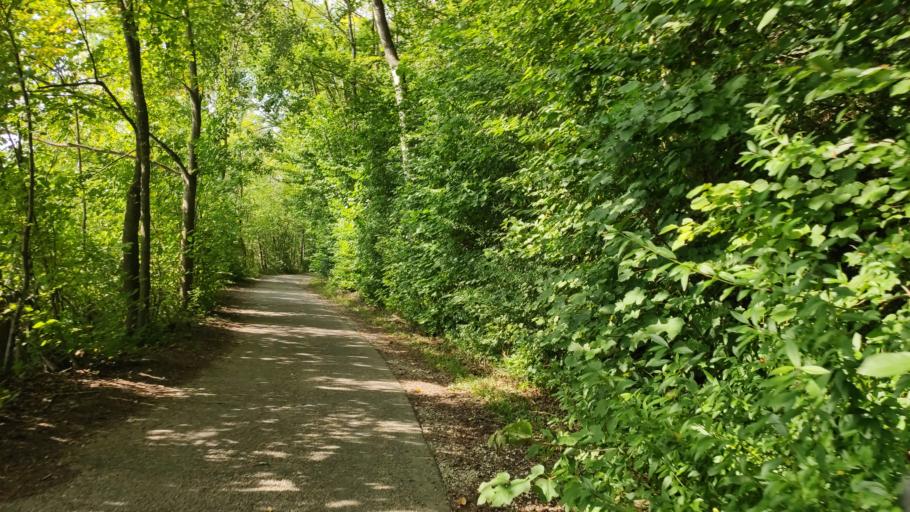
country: DE
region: Bavaria
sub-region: Upper Bavaria
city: Kaufering
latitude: 48.1120
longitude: 10.8675
